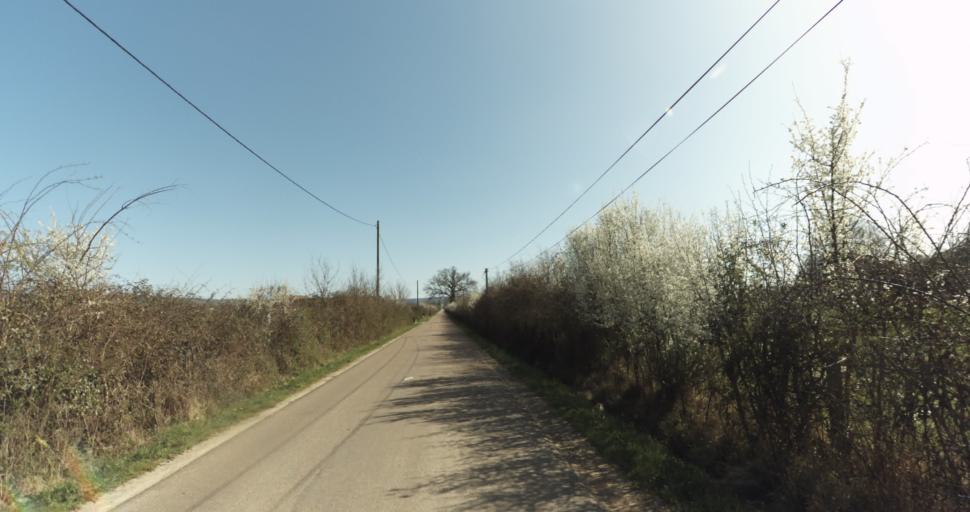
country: FR
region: Lower Normandy
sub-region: Departement du Calvados
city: Saint-Pierre-sur-Dives
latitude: 48.9538
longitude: 0.0104
